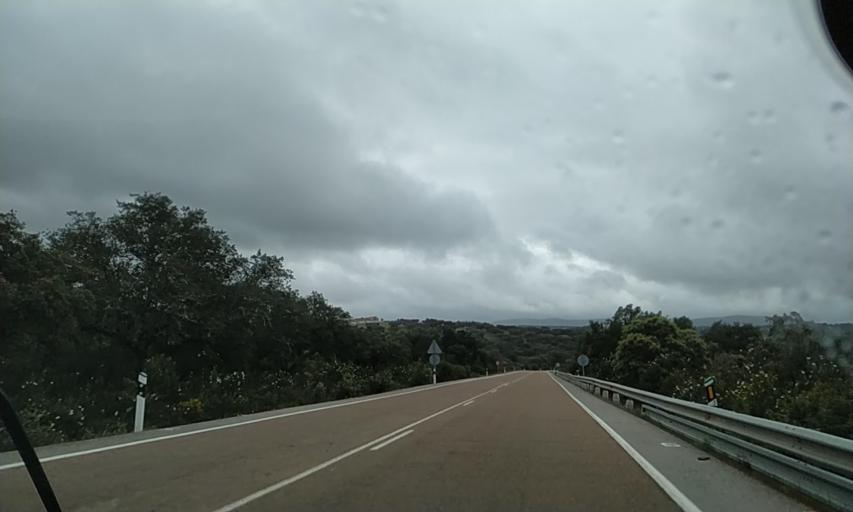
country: ES
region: Extremadura
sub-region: Provincia de Badajoz
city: Puebla de Obando
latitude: 39.2607
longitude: -6.5530
